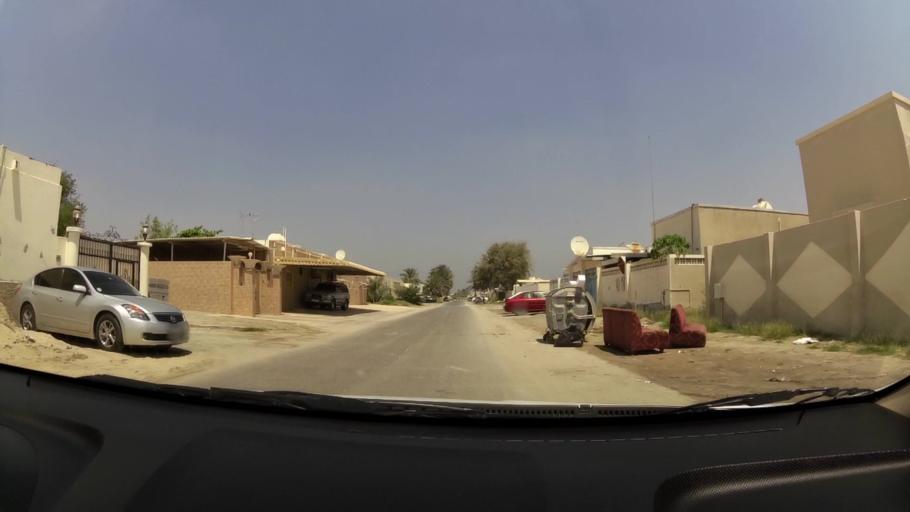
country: AE
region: Umm al Qaywayn
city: Umm al Qaywayn
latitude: 25.5589
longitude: 55.5566
